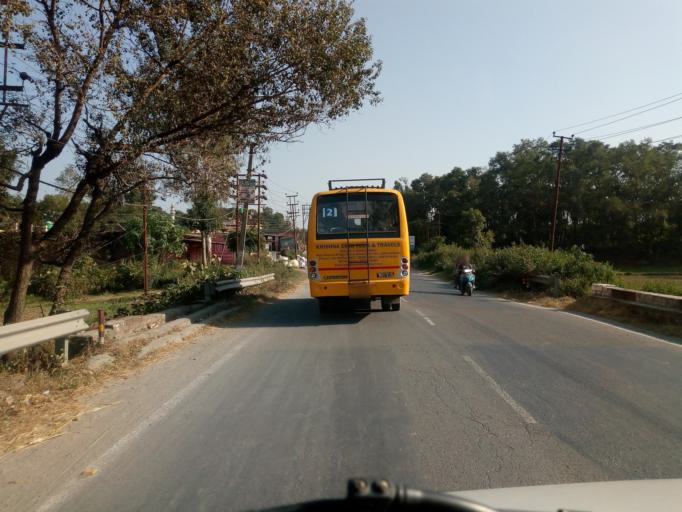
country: IN
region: Uttarakhand
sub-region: Dehradun
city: Harbatpur
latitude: 30.4051
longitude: 77.7944
